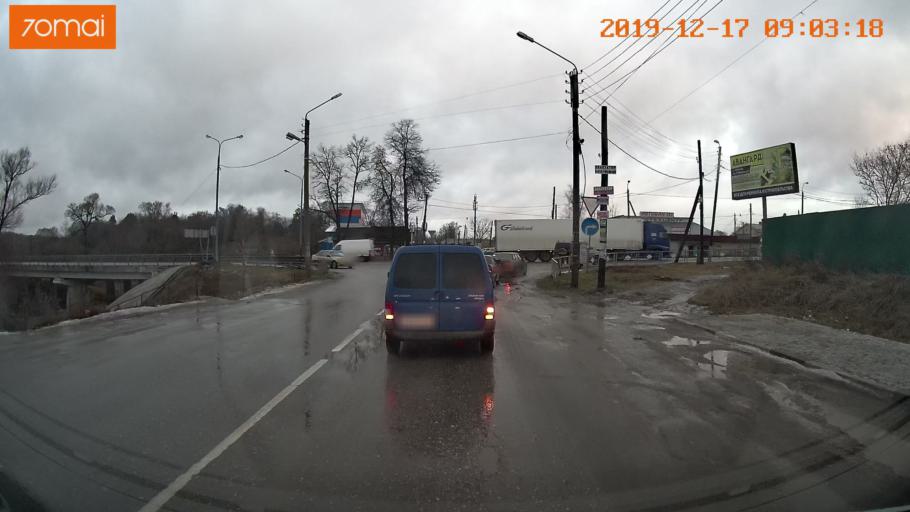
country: RU
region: Vladimir
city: Kosterevo
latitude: 55.9564
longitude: 39.6328
